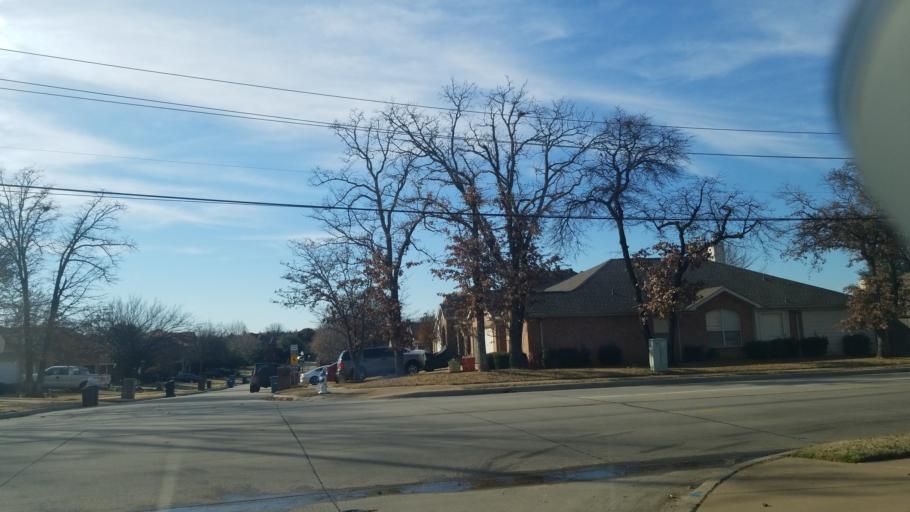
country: US
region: Texas
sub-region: Denton County
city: Corinth
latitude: 33.1406
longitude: -97.0653
